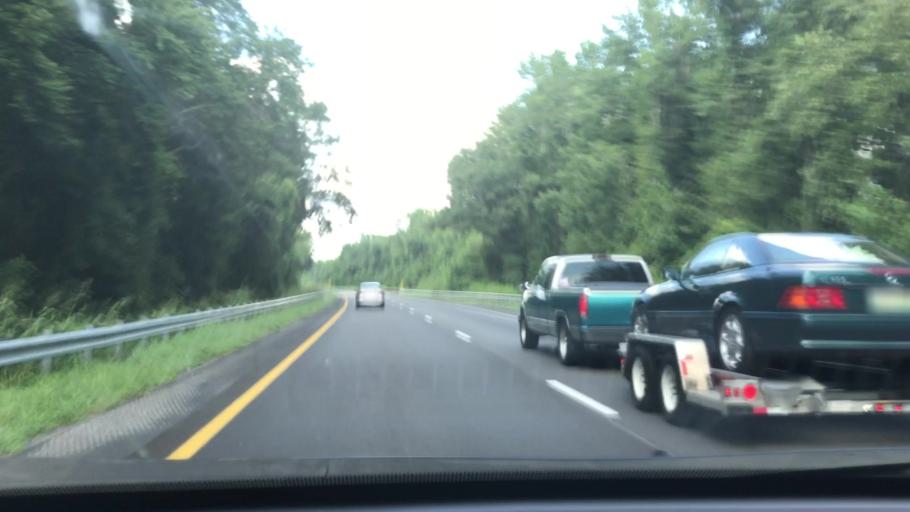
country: US
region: South Carolina
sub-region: Clarendon County
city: Manning
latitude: 33.8221
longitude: -80.1400
